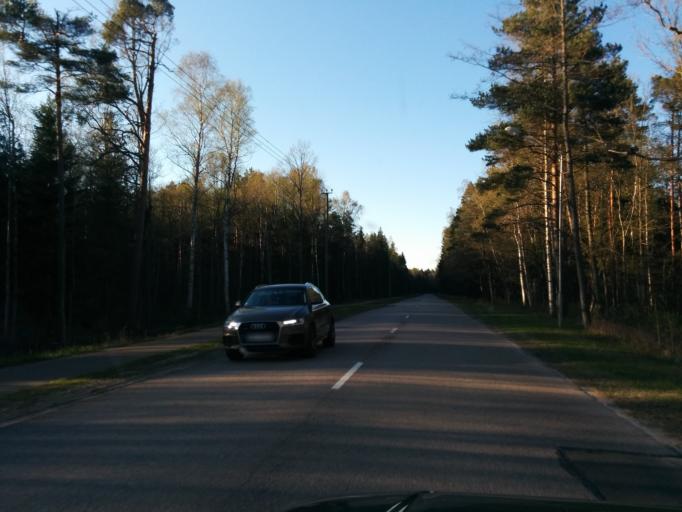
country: LV
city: Tireli
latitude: 56.9548
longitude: 23.5221
